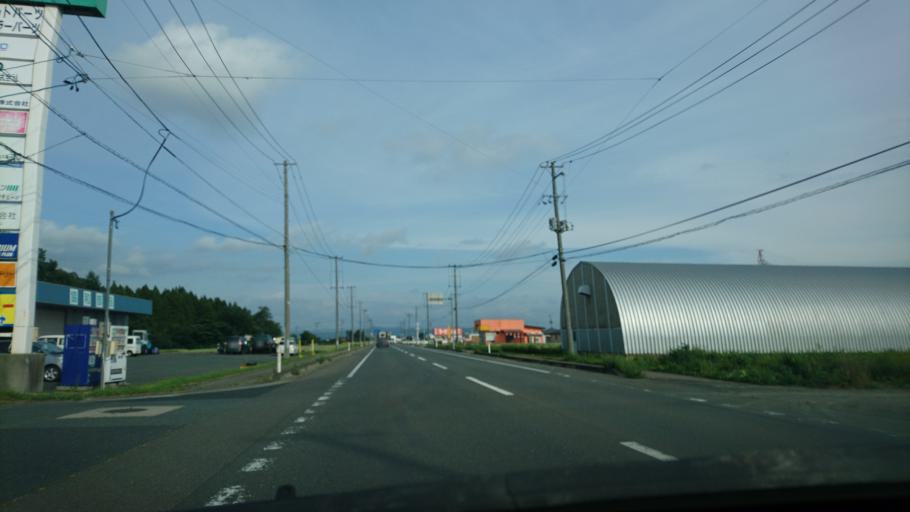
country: JP
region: Iwate
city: Kitakami
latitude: 39.3038
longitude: 141.0400
